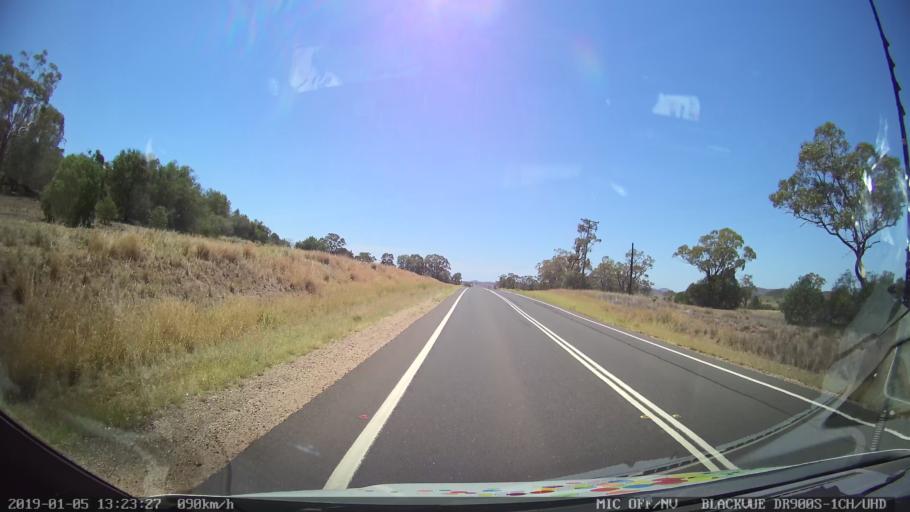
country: AU
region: New South Wales
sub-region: Gunnedah
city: Gunnedah
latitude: -31.0779
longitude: 149.9753
